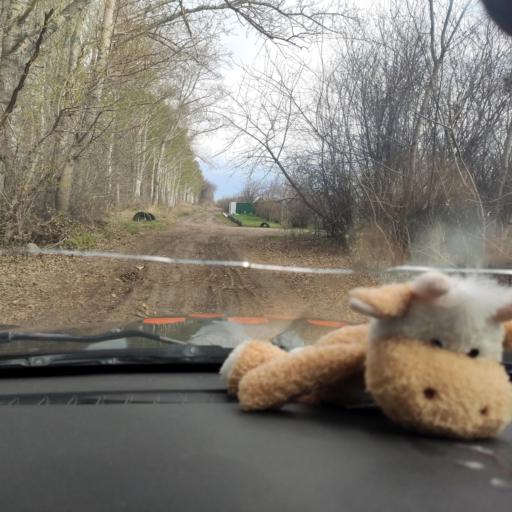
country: RU
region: Samara
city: Tol'yatti
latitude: 53.6053
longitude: 49.2422
